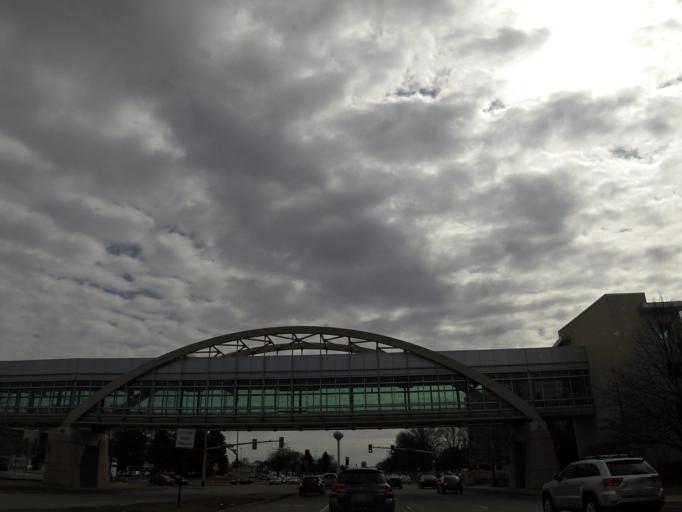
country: US
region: Minnesota
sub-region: Hennepin County
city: Edina
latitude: 44.8865
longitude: -93.3291
